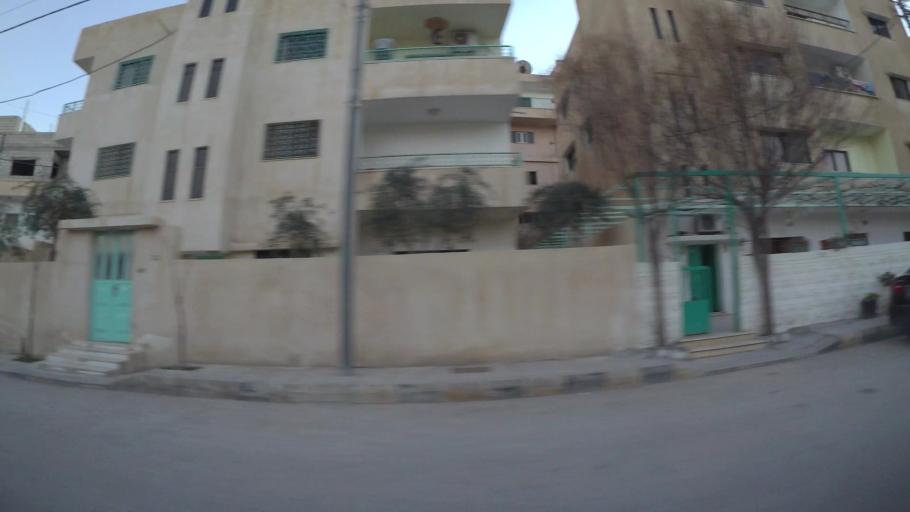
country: JO
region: Ma'an
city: Petra
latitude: 30.3188
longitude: 35.4771
